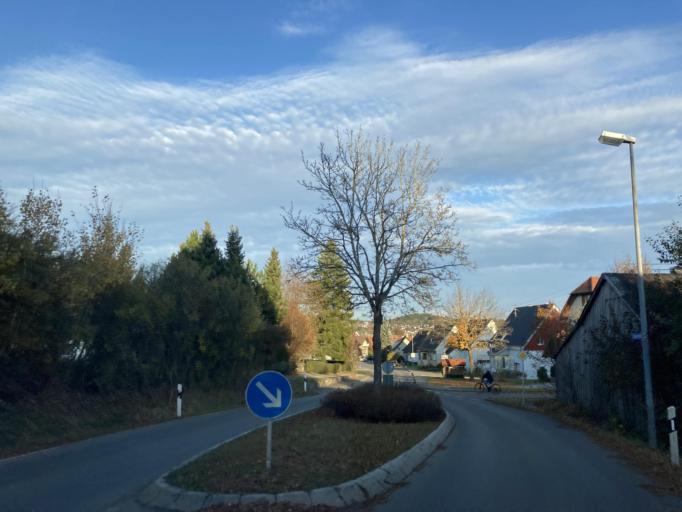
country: DE
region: Baden-Wuerttemberg
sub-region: Freiburg Region
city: Villingen-Schwenningen
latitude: 48.0104
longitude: 8.4484
